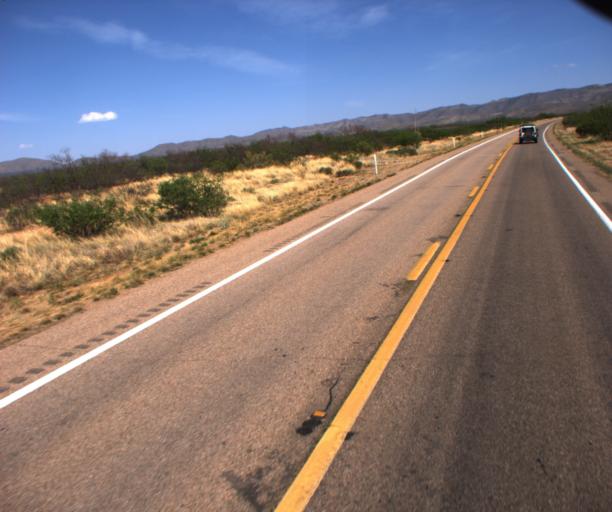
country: US
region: Arizona
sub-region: Cochise County
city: Sierra Vista Southeast
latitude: 31.5423
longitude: -110.0791
